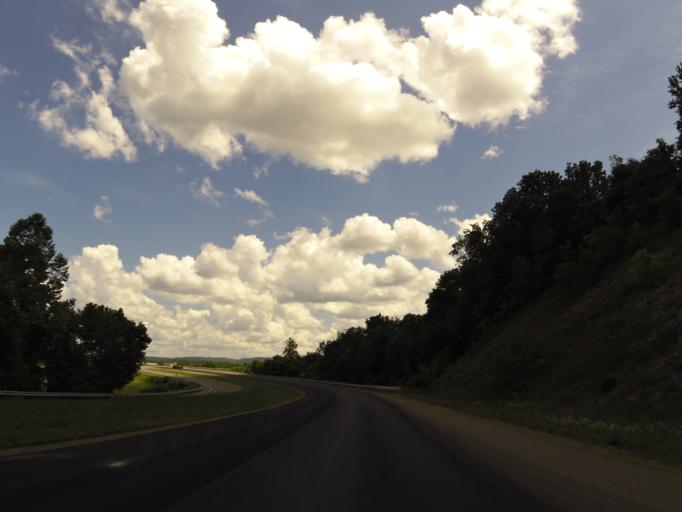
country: US
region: Virginia
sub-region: Lee County
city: Jonesville
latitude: 36.6725
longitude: -83.2048
